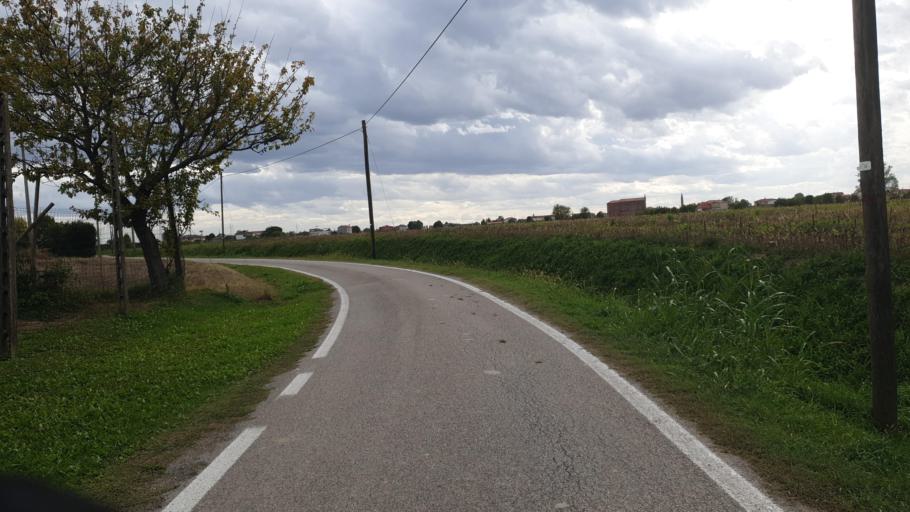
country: IT
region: Veneto
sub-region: Provincia di Padova
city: Polverara
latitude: 45.2810
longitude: 11.9642
